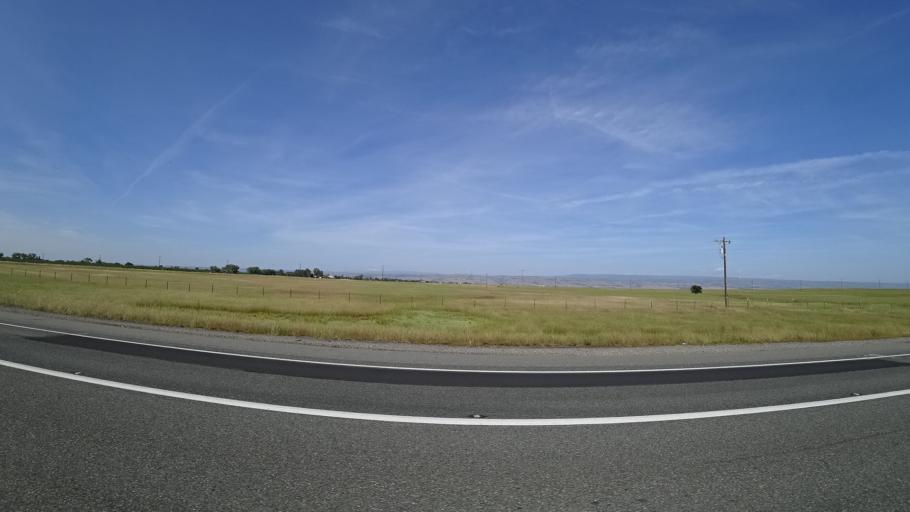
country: US
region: California
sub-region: Tehama County
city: Los Molinos
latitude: 39.9322
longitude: -122.0336
